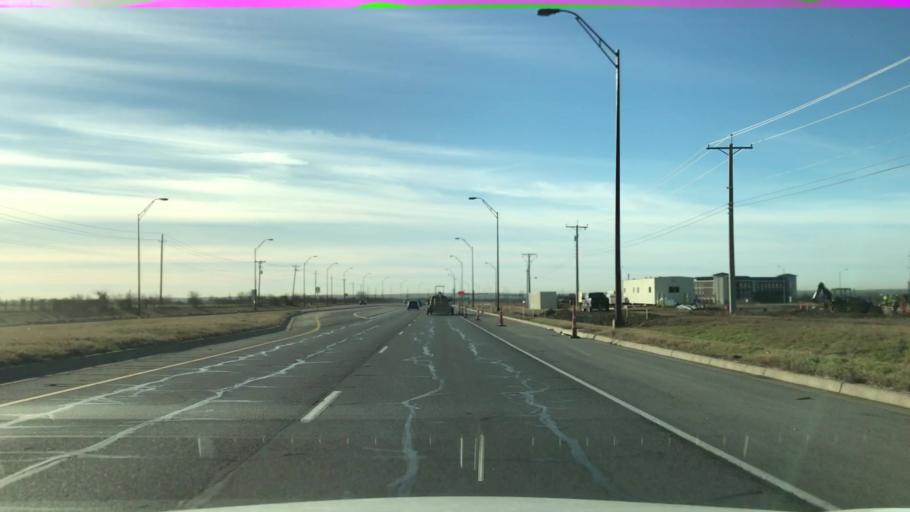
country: US
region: Texas
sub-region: Williamson County
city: Round Rock
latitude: 30.5648
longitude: -97.6477
